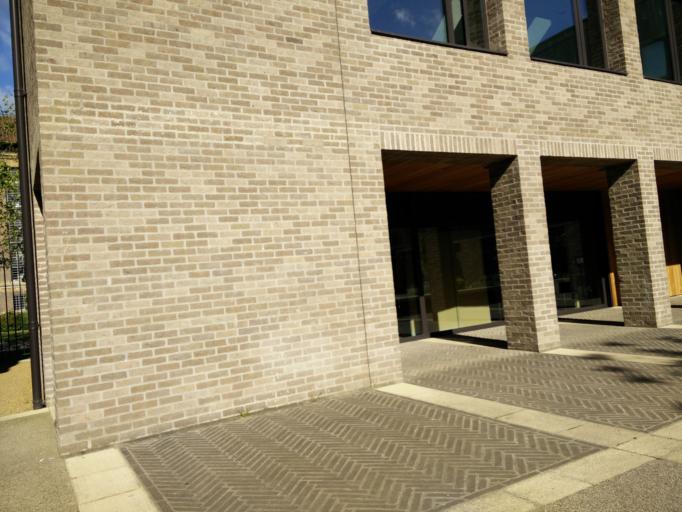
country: GB
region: England
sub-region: Cambridgeshire
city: Cambridge
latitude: 52.2054
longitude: 0.1092
